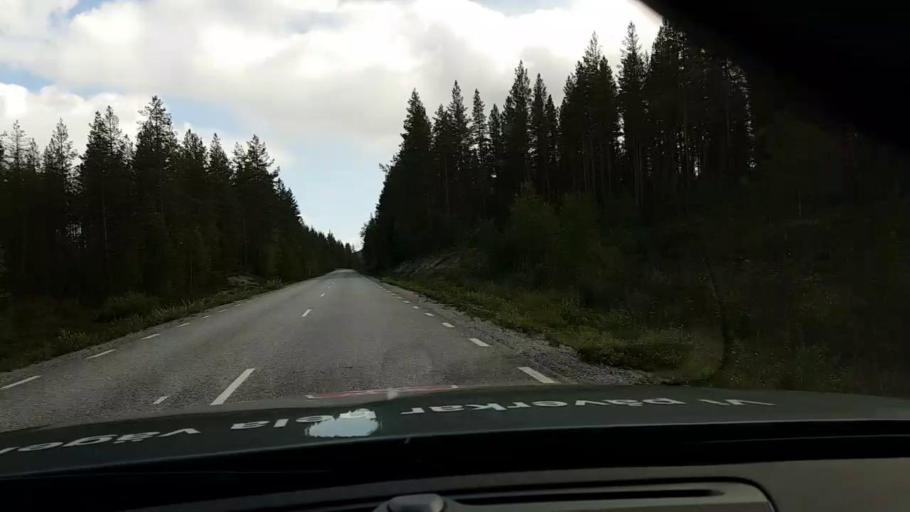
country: SE
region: Vaesternorrland
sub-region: OErnskoeldsviks Kommun
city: Bredbyn
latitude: 63.6939
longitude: 17.7664
